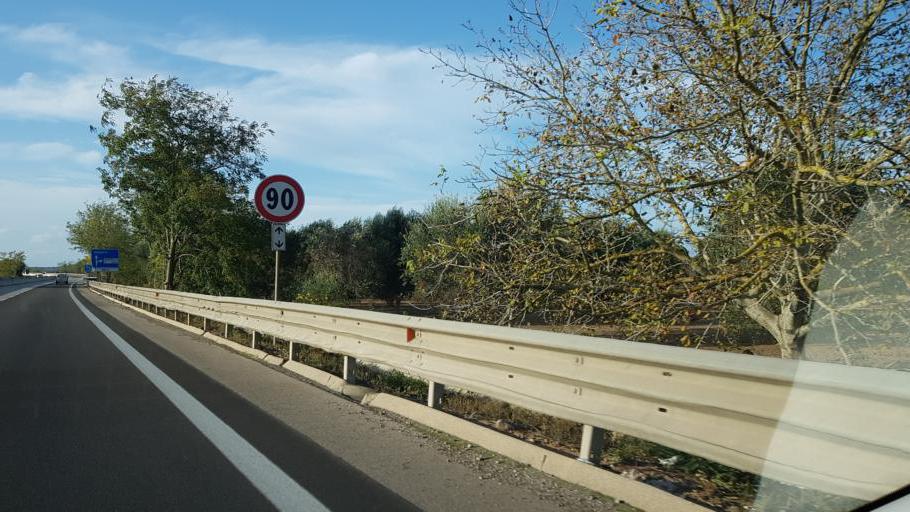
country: IT
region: Apulia
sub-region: Provincia di Brindisi
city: Francavilla Fontana
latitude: 40.5429
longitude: 17.6001
